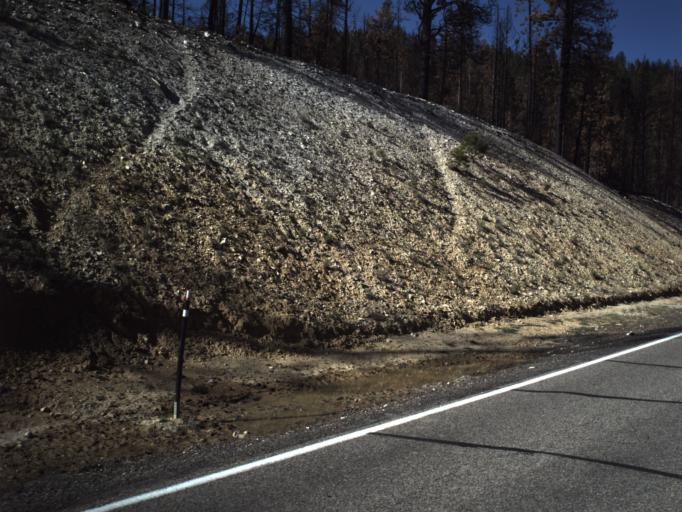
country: US
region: Utah
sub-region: Iron County
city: Parowan
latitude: 37.6533
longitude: -112.6862
